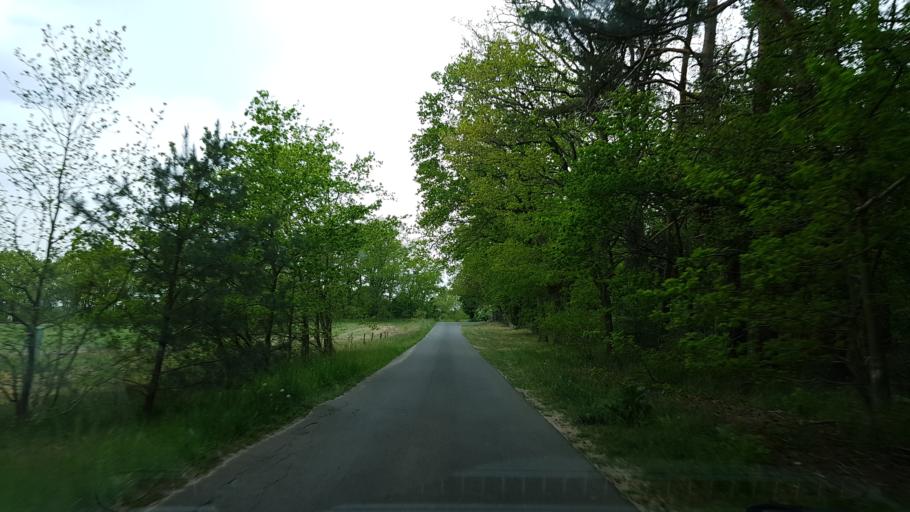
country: DE
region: Lower Saxony
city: Gartow
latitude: 53.0531
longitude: 11.4418
